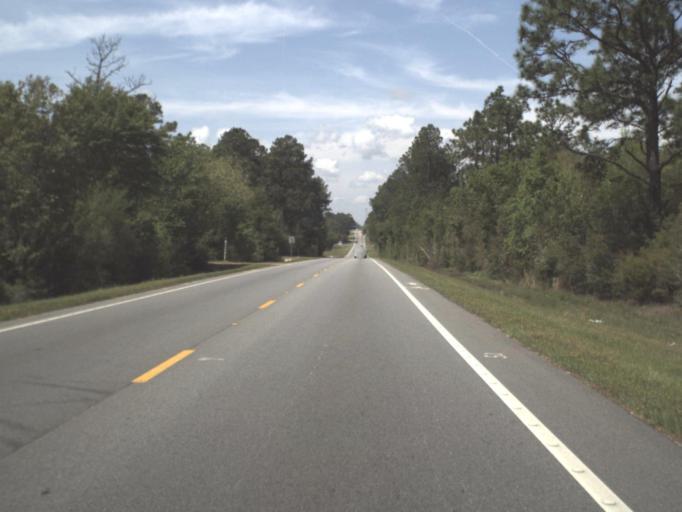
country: US
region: Florida
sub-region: Escambia County
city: Cantonment
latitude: 30.5354
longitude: -87.3682
